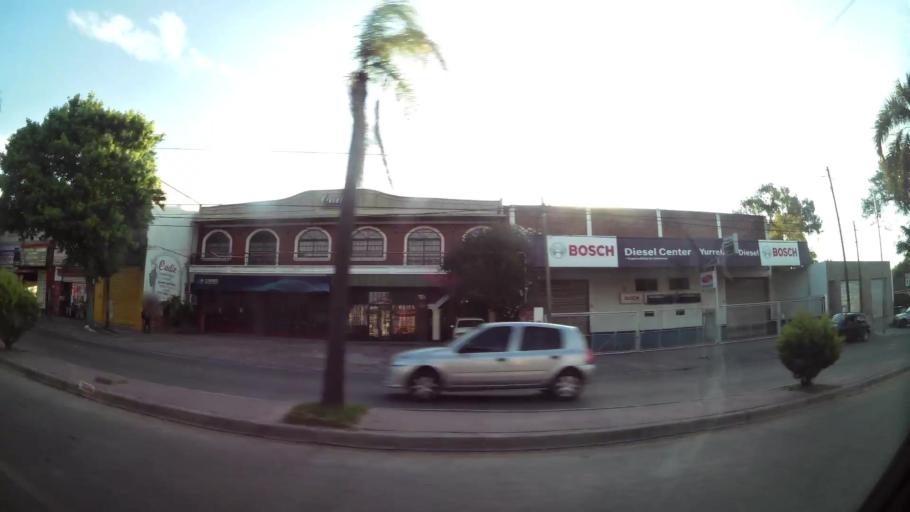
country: AR
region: Buenos Aires
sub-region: Partido de Tigre
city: Tigre
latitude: -34.4552
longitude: -58.6404
